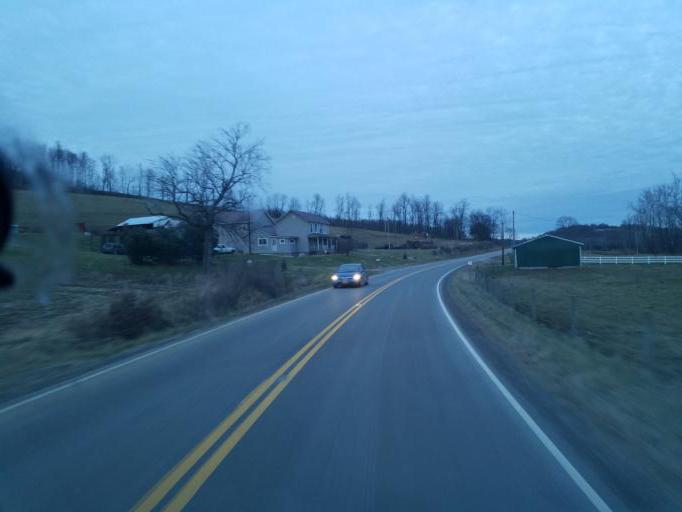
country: US
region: Ohio
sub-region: Muskingum County
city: Dresden
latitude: 40.2469
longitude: -82.0537
